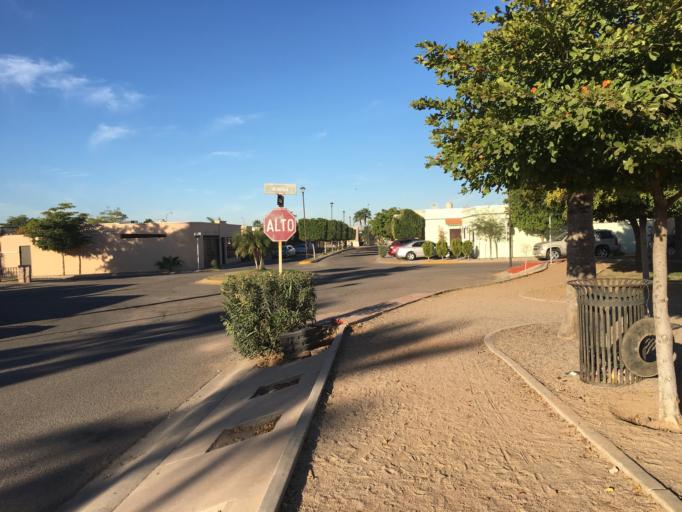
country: MX
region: Sonora
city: Hermosillo
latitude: 29.0898
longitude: -111.0202
